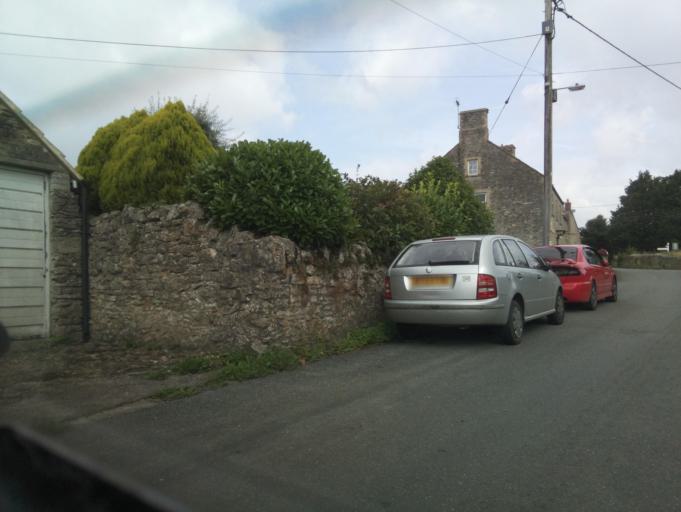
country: GB
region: England
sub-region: Somerset
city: Evercreech
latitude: 51.1514
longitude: -2.4947
